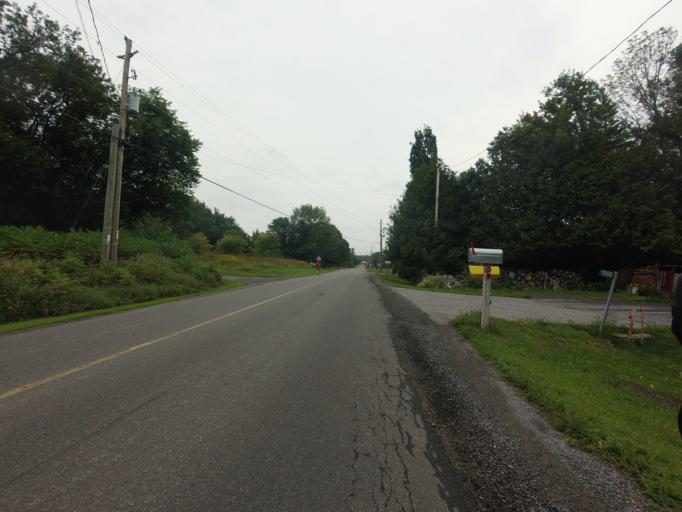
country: CA
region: Ontario
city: Bells Corners
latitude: 45.3399
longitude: -76.0024
